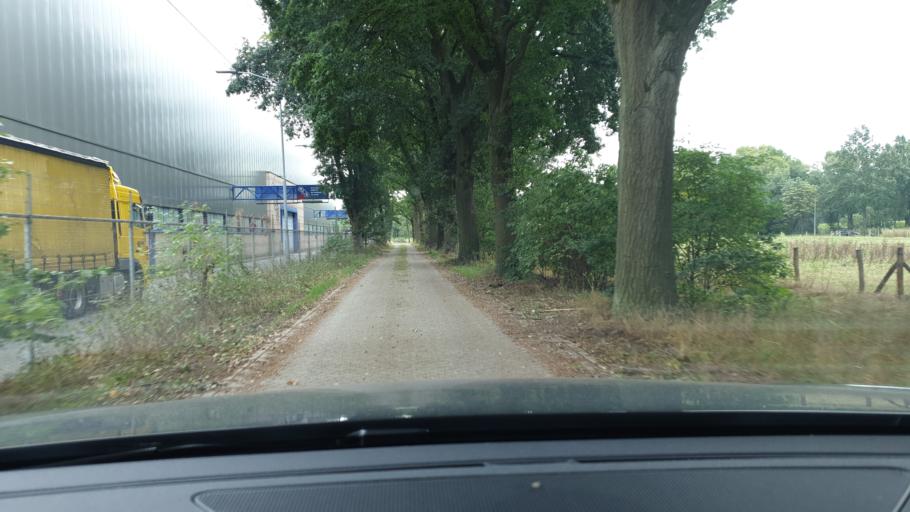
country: NL
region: North Brabant
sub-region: Gemeente Valkenswaard
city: Valkenswaard
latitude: 51.3451
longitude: 5.4815
